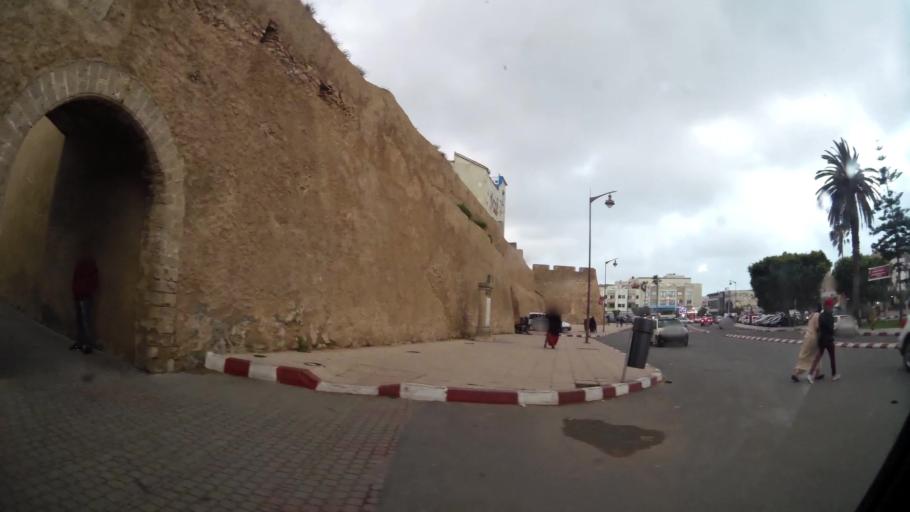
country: MA
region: Doukkala-Abda
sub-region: El-Jadida
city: El Jadida
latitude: 33.2564
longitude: -8.5037
